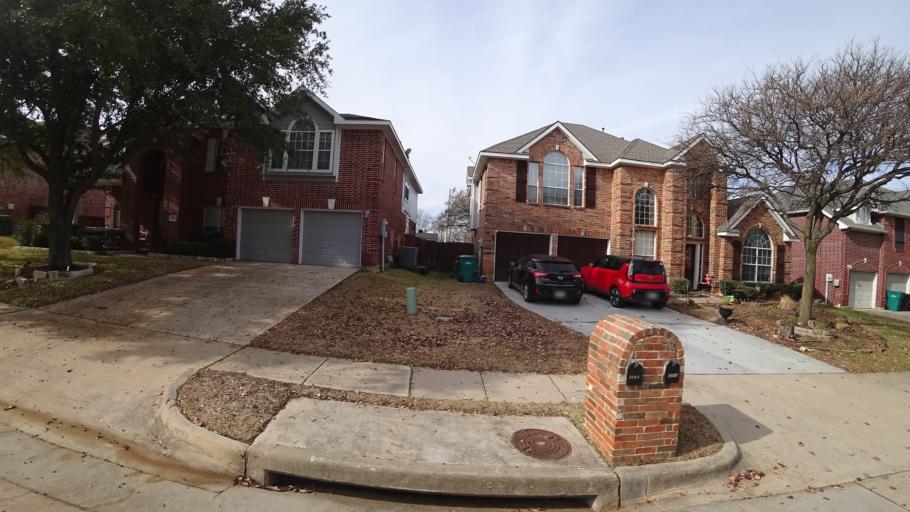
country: US
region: Texas
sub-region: Denton County
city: Highland Village
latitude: 33.0848
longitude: -97.0304
